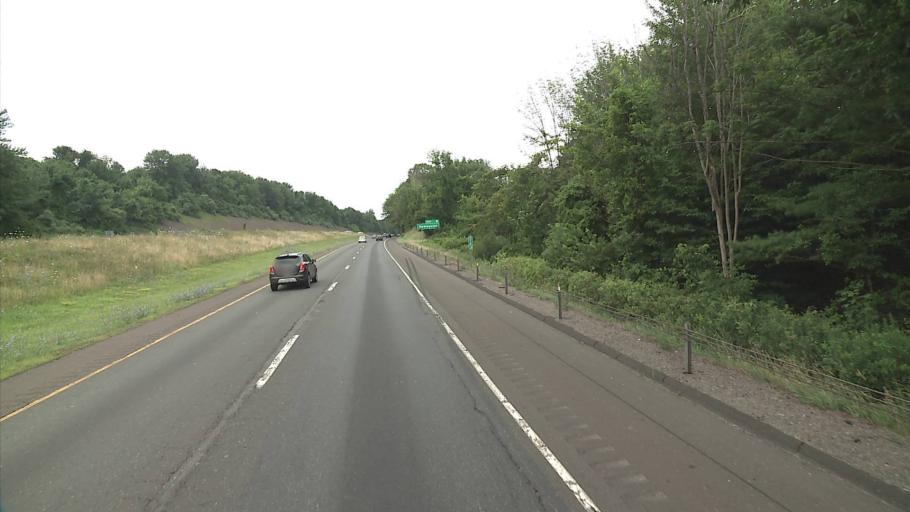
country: US
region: Connecticut
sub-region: Fairfield County
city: Newtown
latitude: 41.4262
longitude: -73.3413
